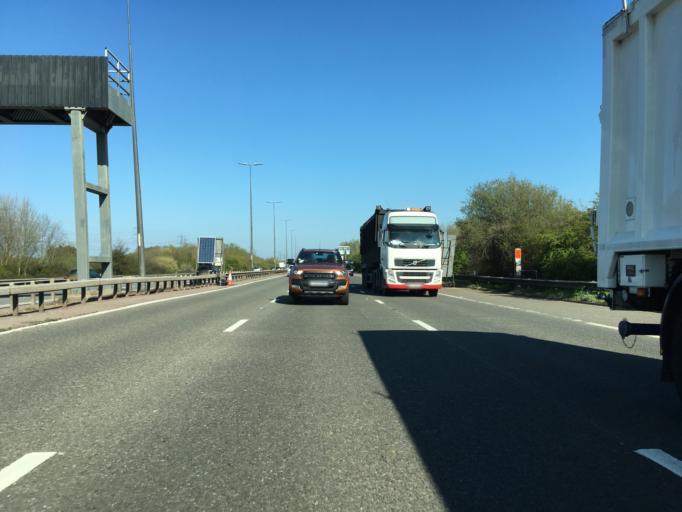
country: GB
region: Wales
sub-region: Monmouthshire
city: Caldicot
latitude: 51.5807
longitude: -2.7578
